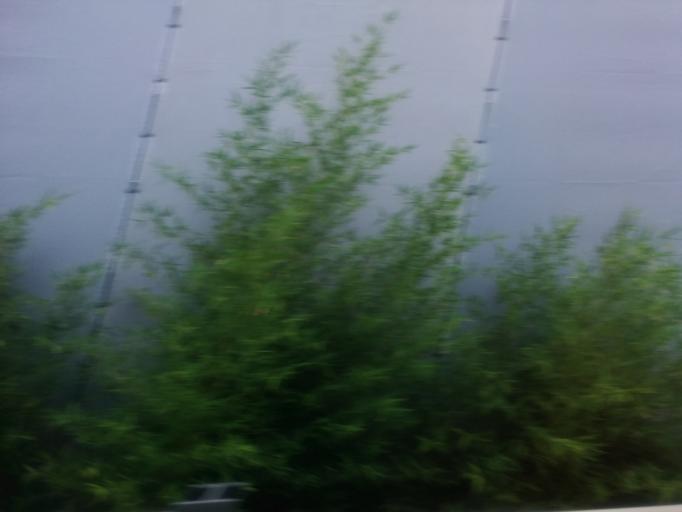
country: JP
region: Kyoto
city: Kyoto
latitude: 34.9715
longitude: 135.7703
